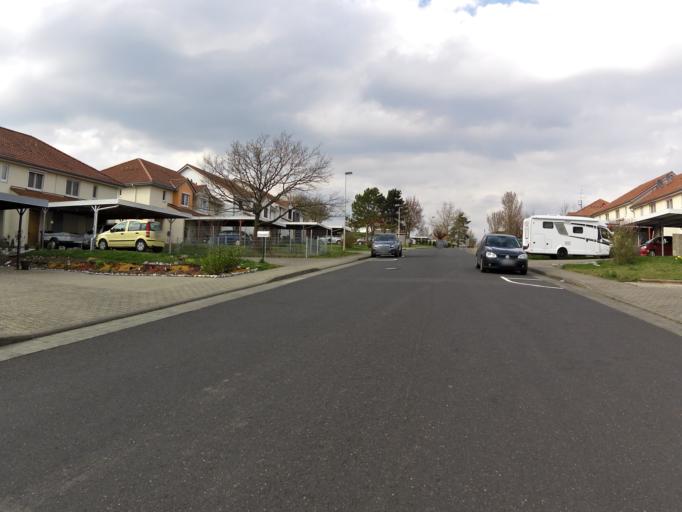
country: DE
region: Bavaria
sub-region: Regierungsbezirk Unterfranken
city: Kitzingen
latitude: 49.7380
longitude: 10.1313
